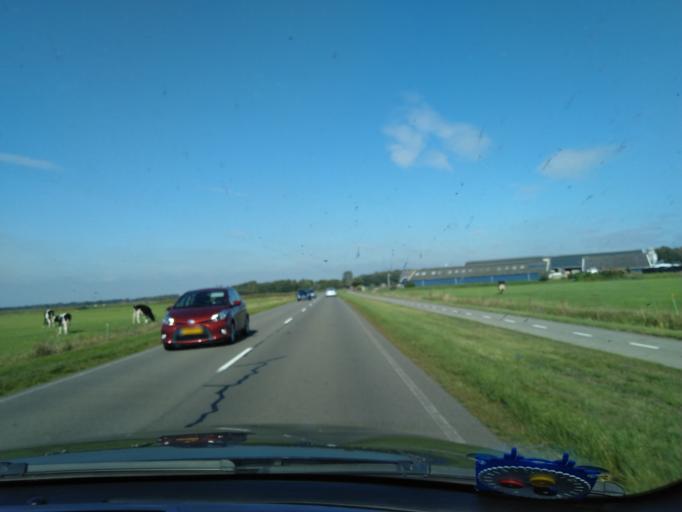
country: NL
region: Drenthe
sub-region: Gemeente Aa en Hunze
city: Anloo
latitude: 53.0688
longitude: 6.7596
